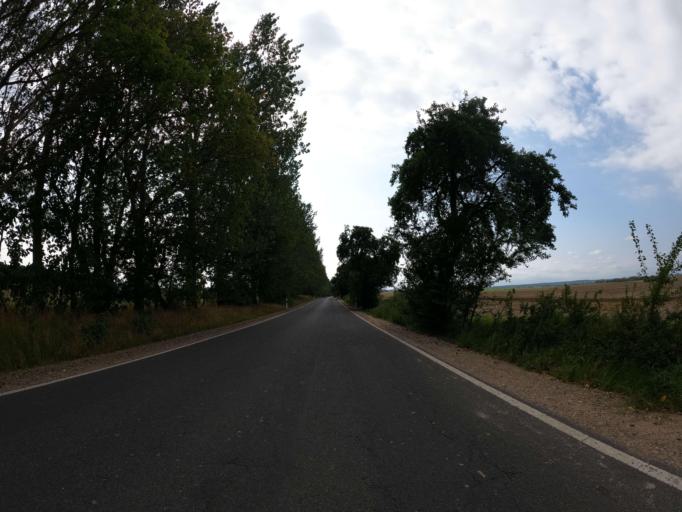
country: DE
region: Mecklenburg-Vorpommern
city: Malchow
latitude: 53.4476
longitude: 12.5110
